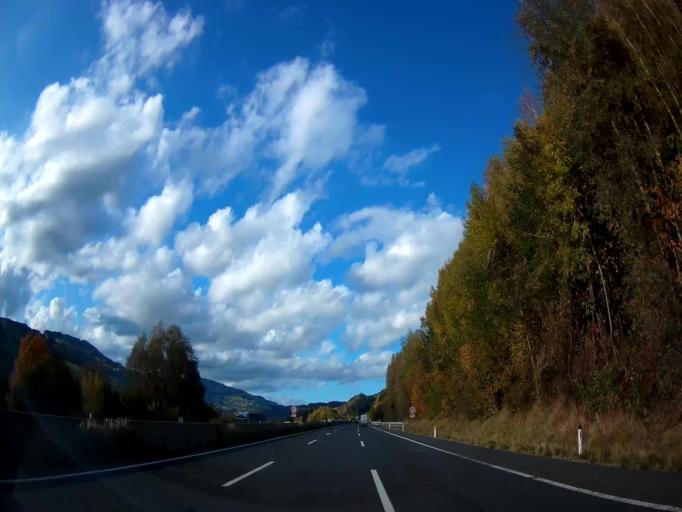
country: AT
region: Carinthia
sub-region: Politischer Bezirk Wolfsberg
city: Wolfsberg
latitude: 46.8753
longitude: 14.8324
